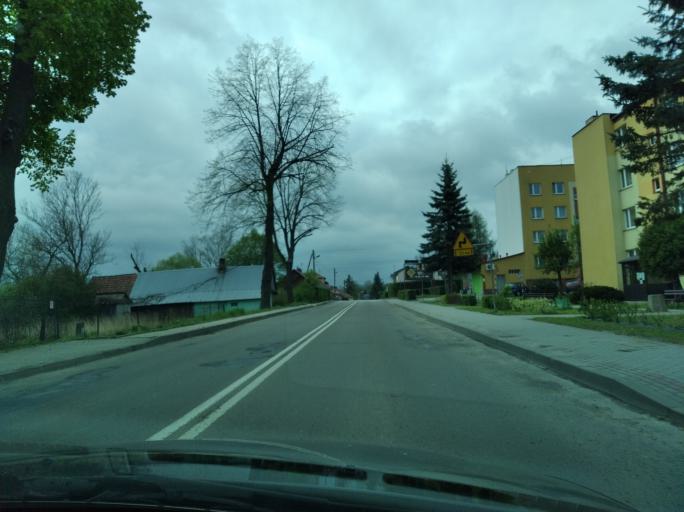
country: PL
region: Subcarpathian Voivodeship
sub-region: Powiat rzeszowski
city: Dynow
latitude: 49.8201
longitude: 22.2347
